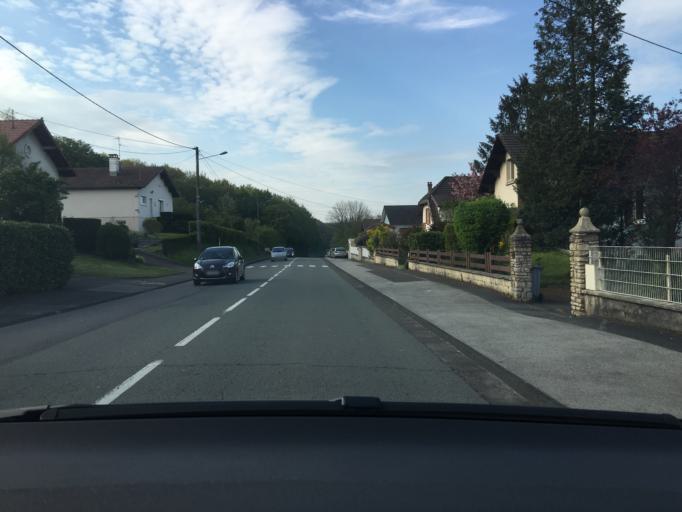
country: FR
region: Franche-Comte
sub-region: Departement du Doubs
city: Courcelles-les-Montbeliard
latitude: 47.4967
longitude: 6.7806
